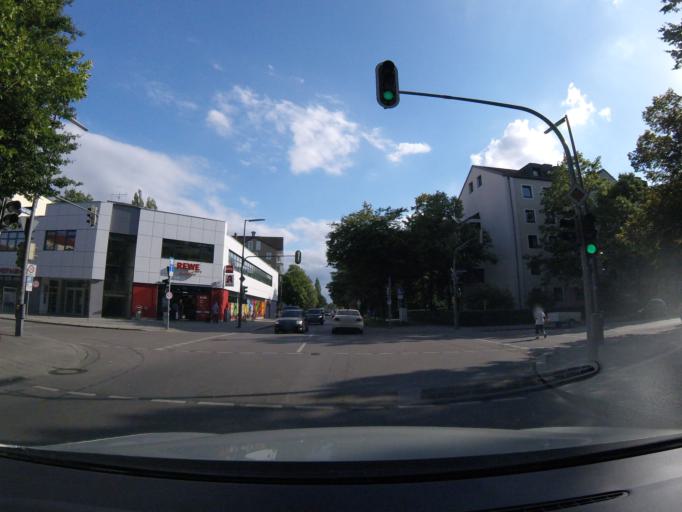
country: DE
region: Bavaria
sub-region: Upper Bavaria
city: Bogenhausen
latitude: 48.1286
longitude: 11.6461
